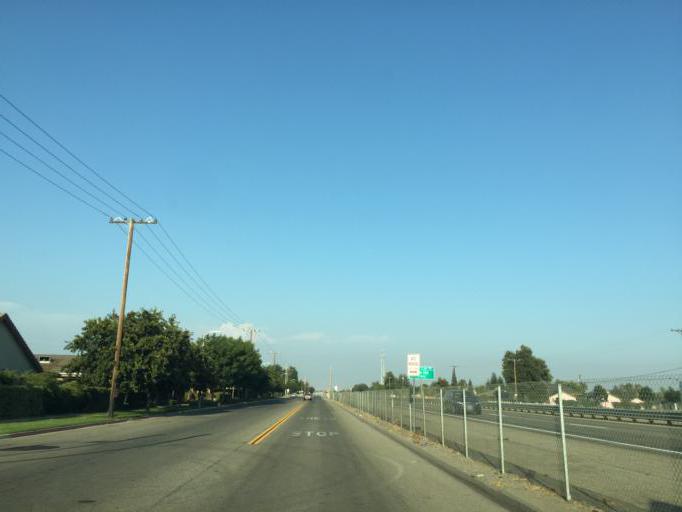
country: US
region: California
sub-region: Tulare County
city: Visalia
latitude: 36.3273
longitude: -119.2500
